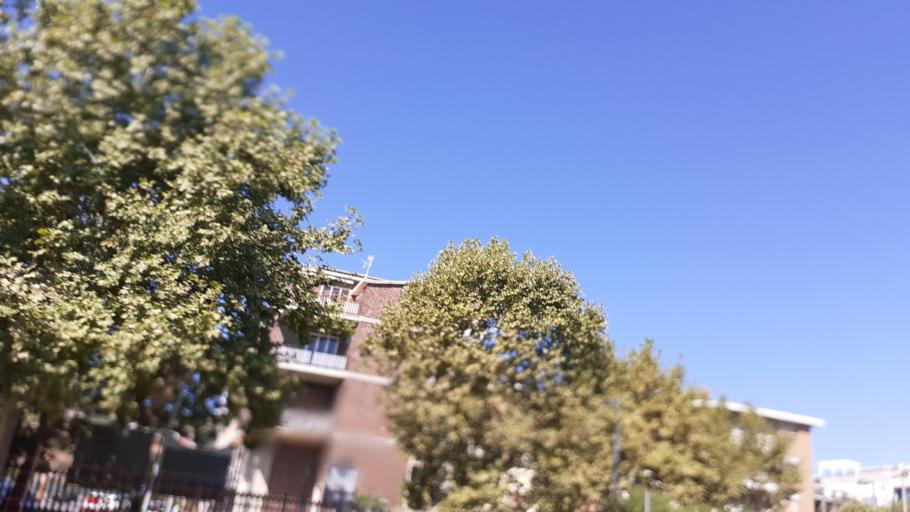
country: IT
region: Abruzzo
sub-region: Provincia di Chieti
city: Marina di Vasto
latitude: 42.1027
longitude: 14.7172
